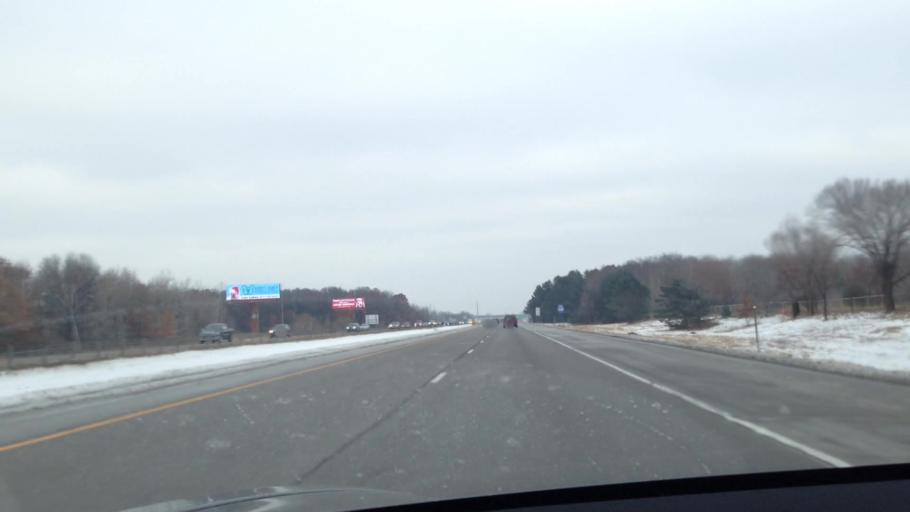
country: US
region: Minnesota
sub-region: Anoka County
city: Lexington
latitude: 45.1479
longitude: -93.1789
